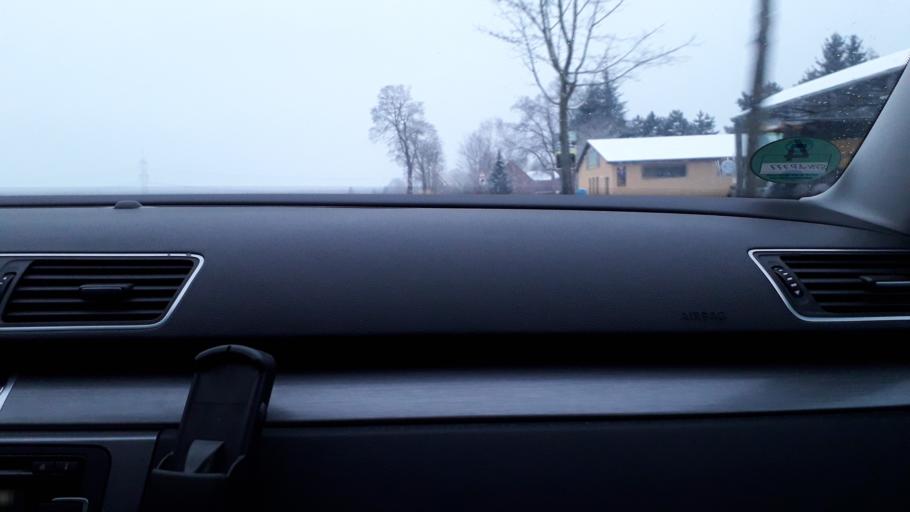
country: DE
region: Brandenburg
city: Spremberg
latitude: 51.5979
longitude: 14.4500
